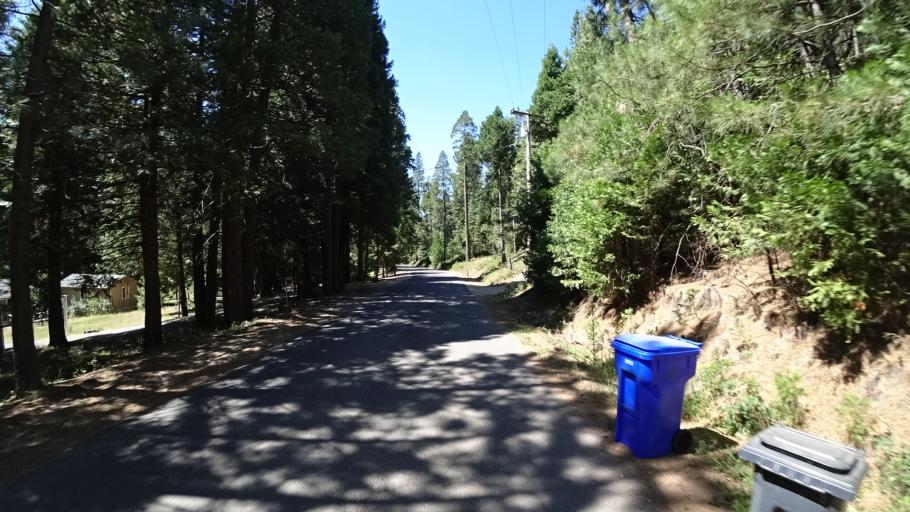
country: US
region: California
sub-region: Amador County
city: Pioneer
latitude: 38.4407
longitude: -120.4314
